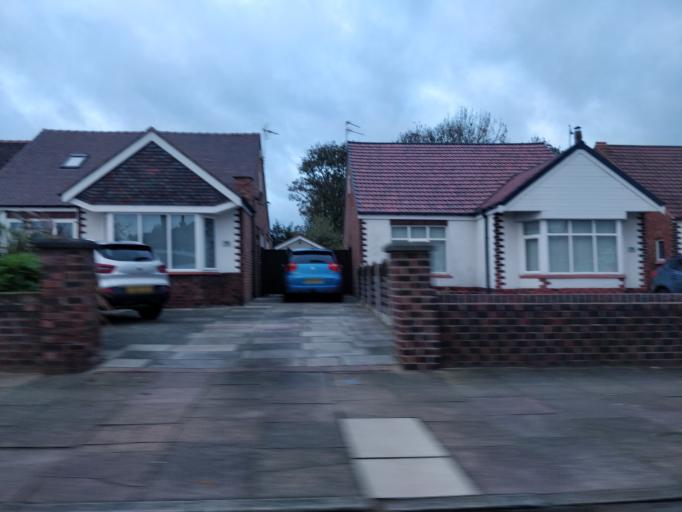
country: GB
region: England
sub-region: Sefton
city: Southport
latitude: 53.6652
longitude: -2.9751
